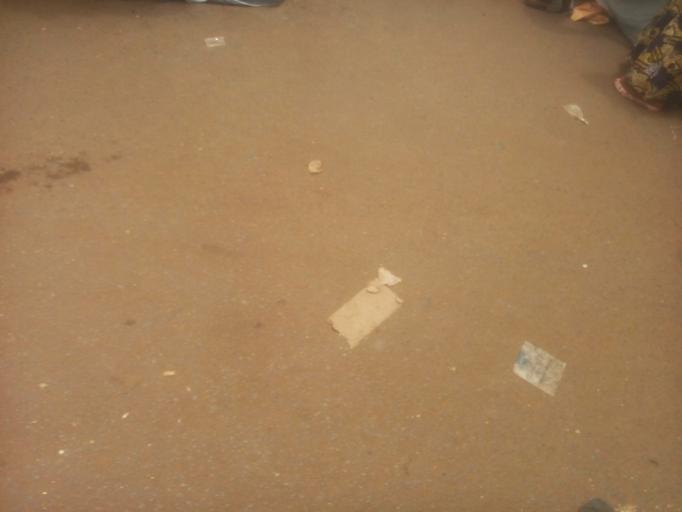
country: ML
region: Bamako
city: Bamako
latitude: 12.6479
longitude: -7.9931
